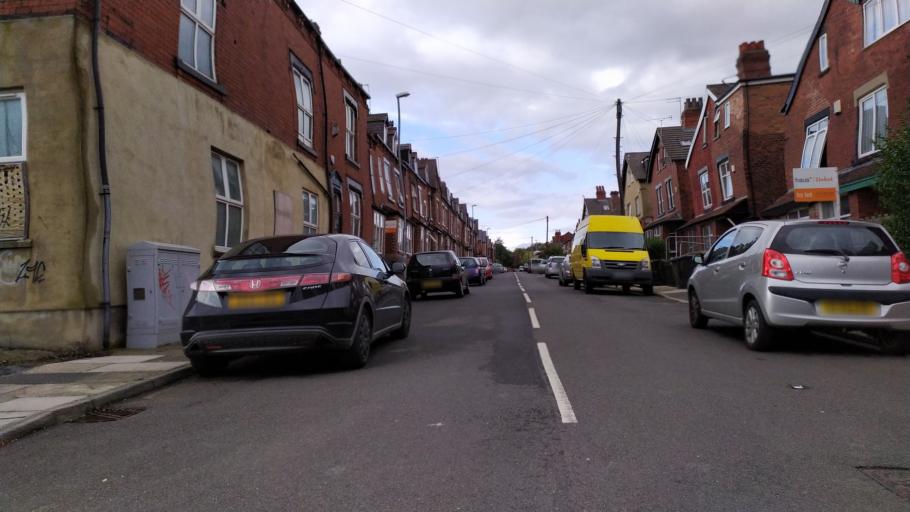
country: GB
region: England
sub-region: City and Borough of Leeds
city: Chapel Allerton
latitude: 53.8167
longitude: -1.5513
